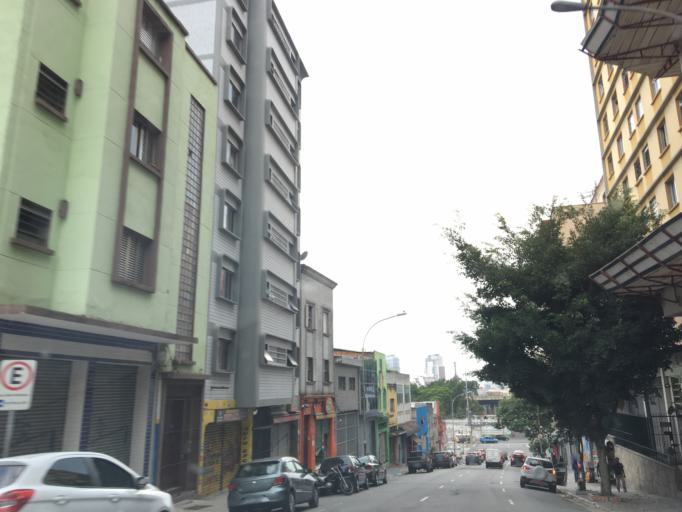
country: BR
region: Sao Paulo
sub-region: Sao Paulo
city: Sao Paulo
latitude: -23.5523
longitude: -46.6288
